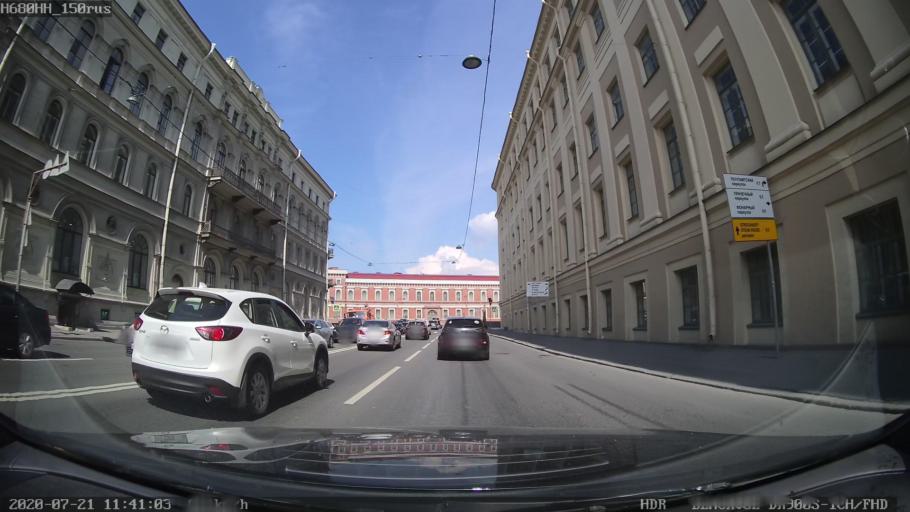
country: RU
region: St.-Petersburg
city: Saint Petersburg
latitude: 59.9274
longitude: 30.2958
